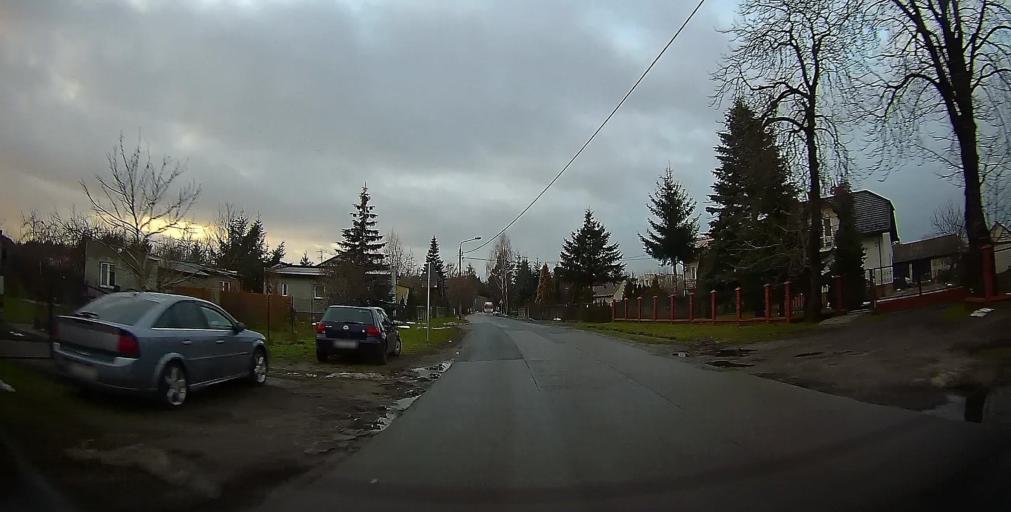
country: PL
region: Masovian Voivodeship
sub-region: Radom
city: Radom
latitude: 51.4494
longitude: 21.1368
